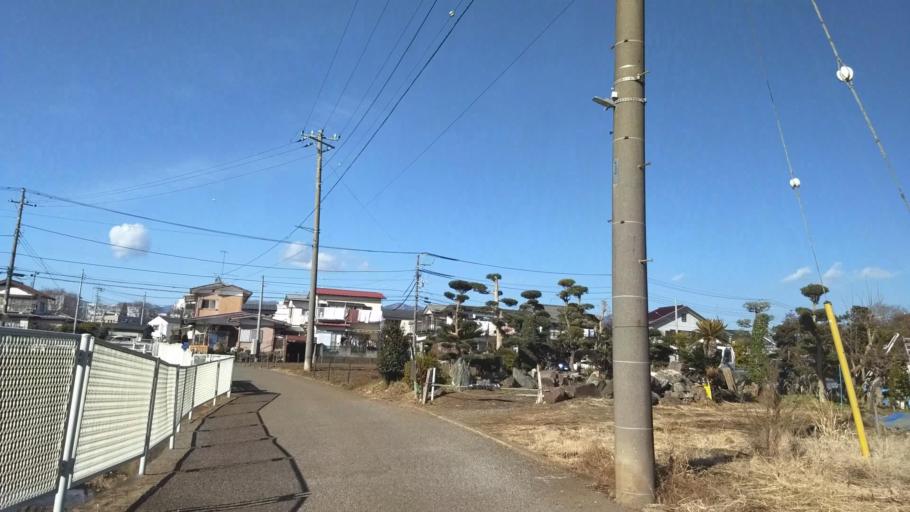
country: JP
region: Kanagawa
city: Hadano
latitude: 35.3440
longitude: 139.2361
